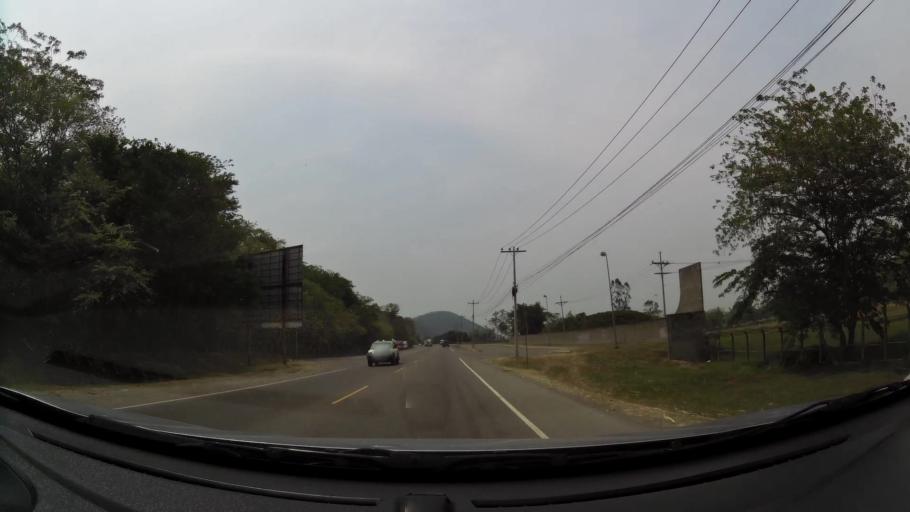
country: HN
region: Cortes
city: Bejuco
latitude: 15.1637
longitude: -87.9481
